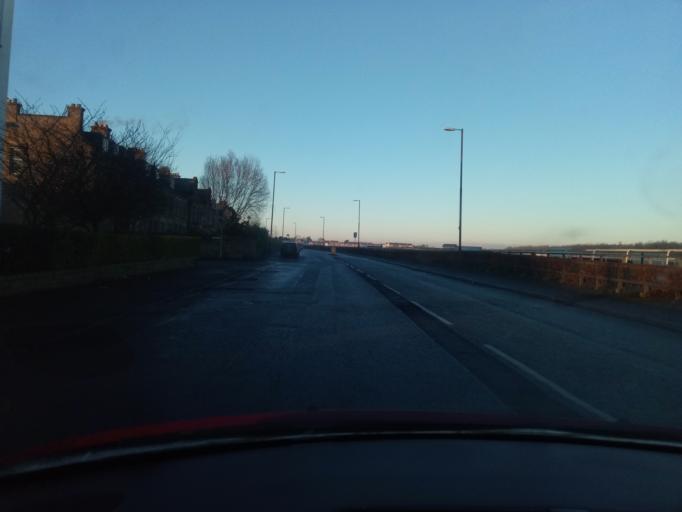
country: GB
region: Scotland
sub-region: East Lothian
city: Musselburgh
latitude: 55.9453
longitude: -3.0334
